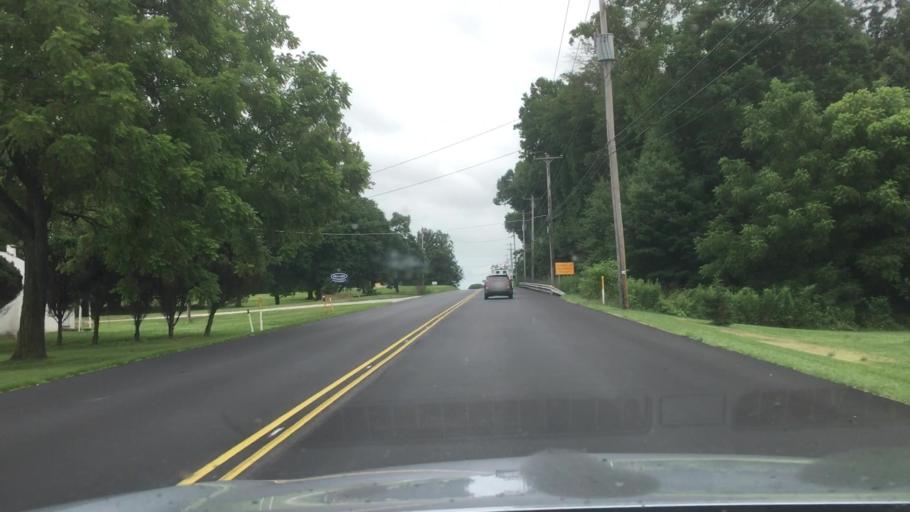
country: US
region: Pennsylvania
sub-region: Chester County
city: West Grove
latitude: 39.8772
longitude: -75.8903
